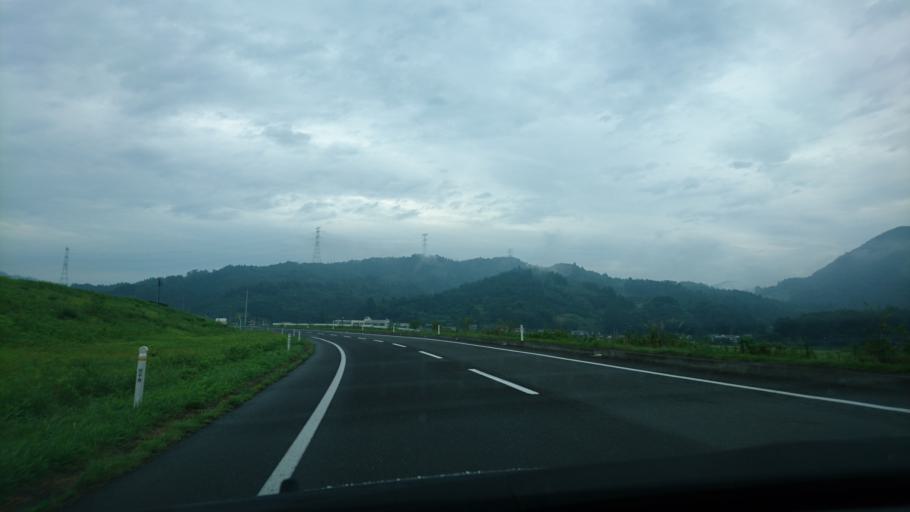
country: JP
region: Iwate
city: Ichinoseki
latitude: 38.9269
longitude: 141.2578
